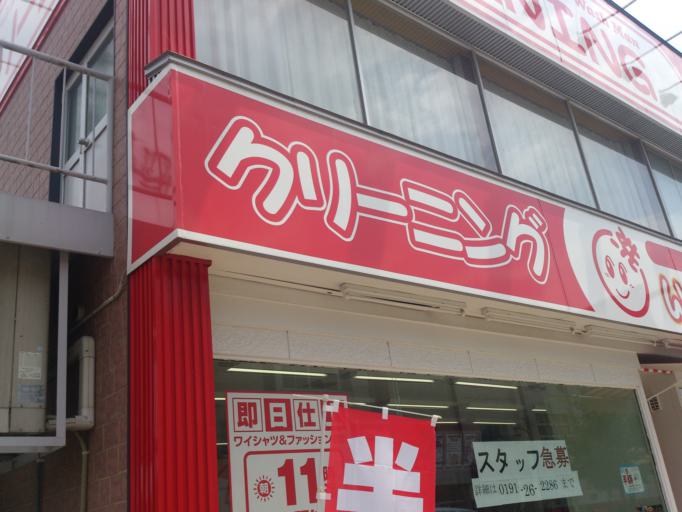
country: JP
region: Iwate
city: Ichinoseki
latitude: 38.9271
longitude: 141.1349
